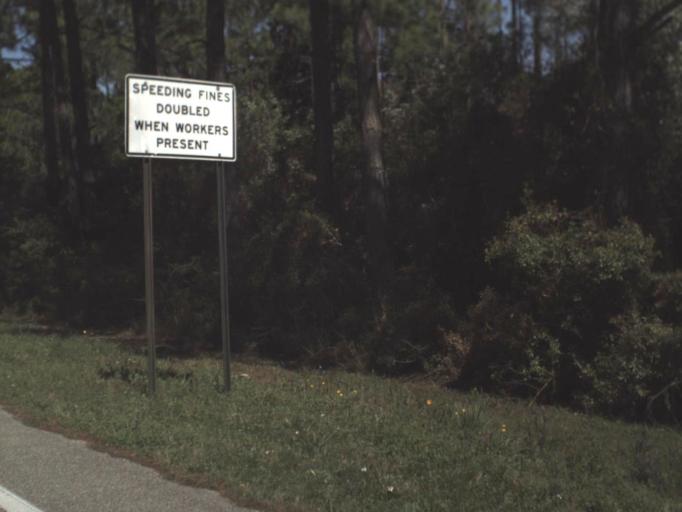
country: US
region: Florida
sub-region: Gulf County
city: Port Saint Joe
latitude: 29.7786
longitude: -85.2987
